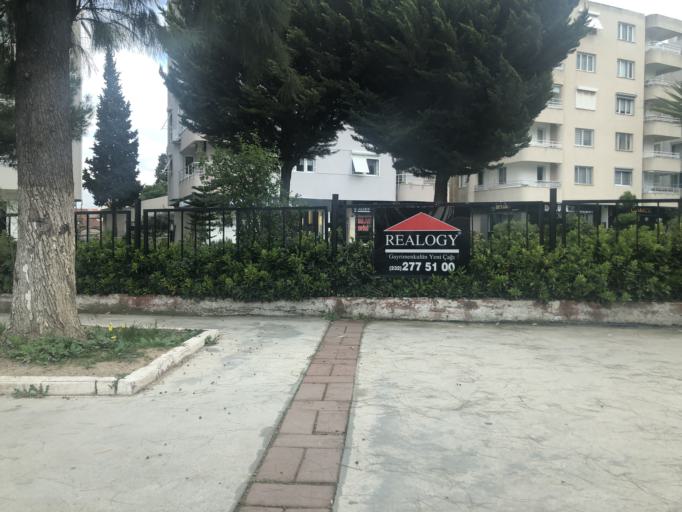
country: TR
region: Izmir
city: Karsiyaka
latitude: 38.3938
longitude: 27.0452
